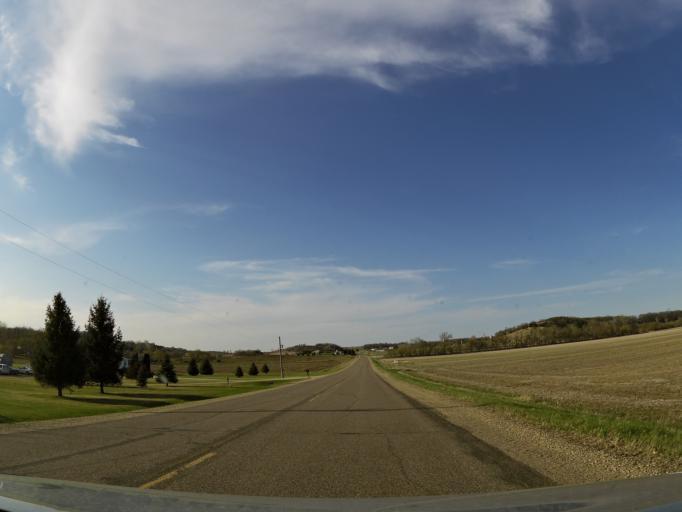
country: US
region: Wisconsin
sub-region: Pierce County
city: River Falls
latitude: 44.7609
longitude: -92.6396
